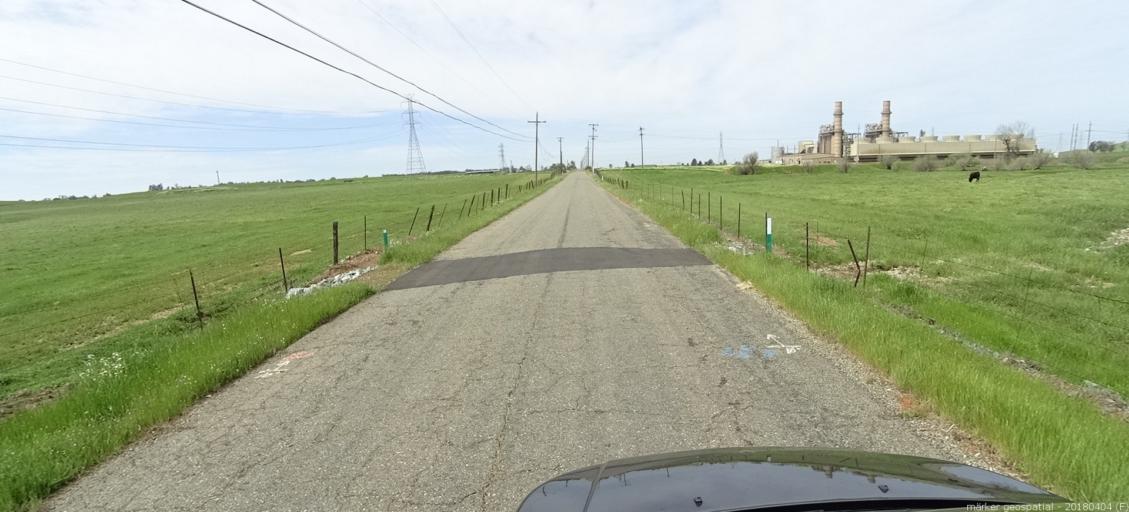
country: US
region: California
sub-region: Sacramento County
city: Clay
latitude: 38.3362
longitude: -121.1184
